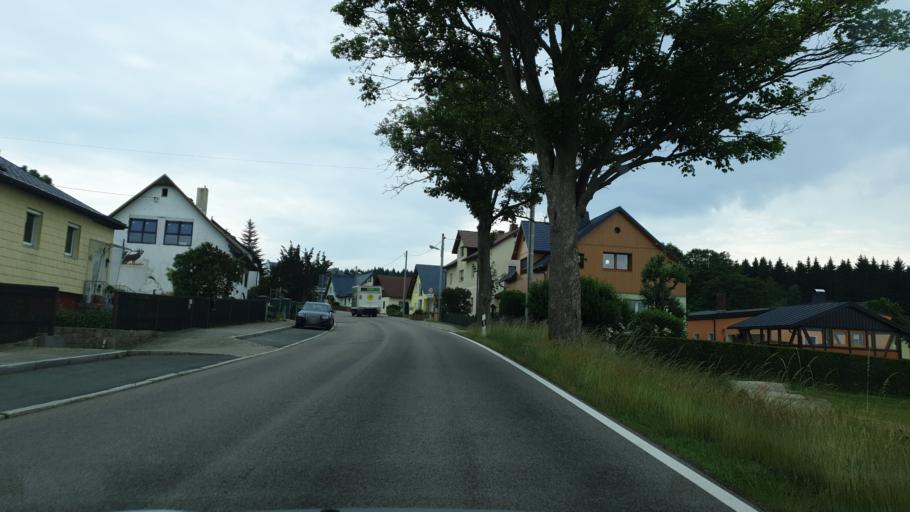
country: DE
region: Saxony
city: Auerbach
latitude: 50.4888
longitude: 12.4304
